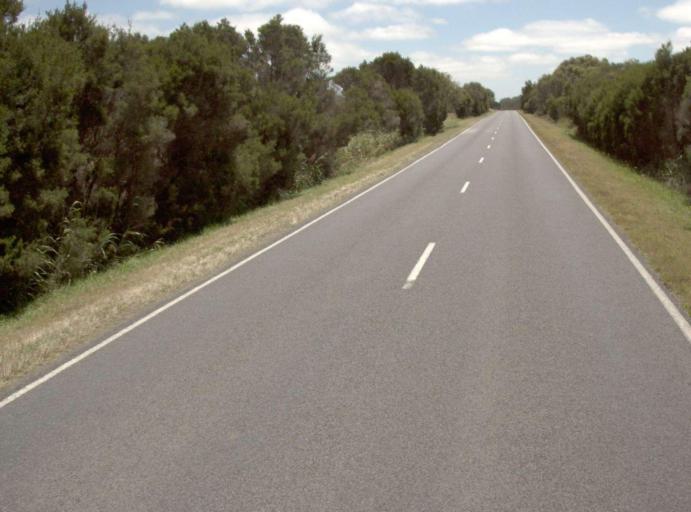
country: AU
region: Victoria
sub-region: Bass Coast
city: North Wonthaggi
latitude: -38.6362
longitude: 146.0118
